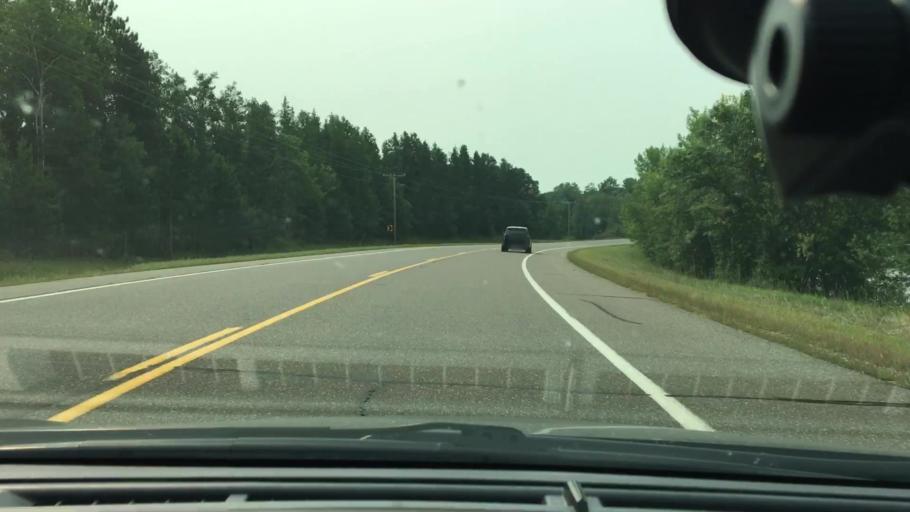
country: US
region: Minnesota
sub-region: Crow Wing County
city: Cross Lake
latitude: 46.5682
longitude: -94.1287
